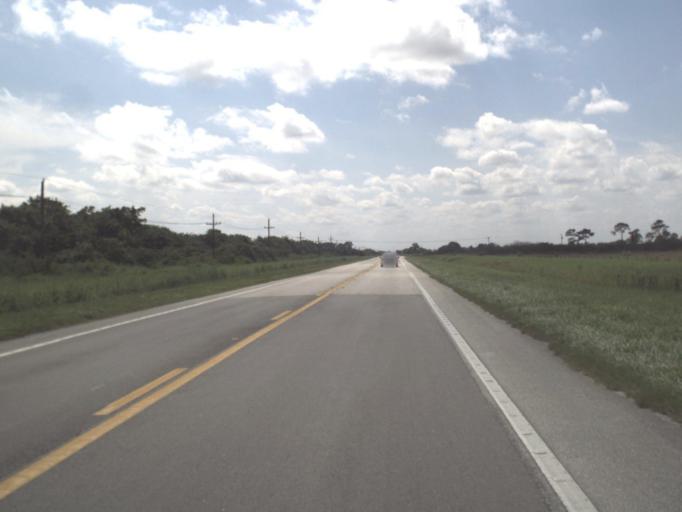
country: US
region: Florida
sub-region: Hendry County
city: Port LaBelle
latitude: 26.6510
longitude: -81.4362
